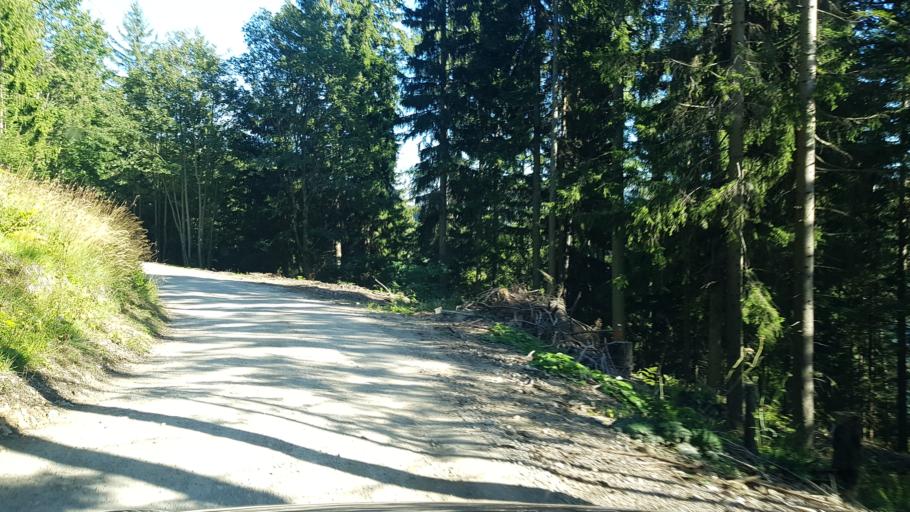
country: SI
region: Ravne na Koroskem
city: Kotlje
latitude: 46.4807
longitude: 14.9444
